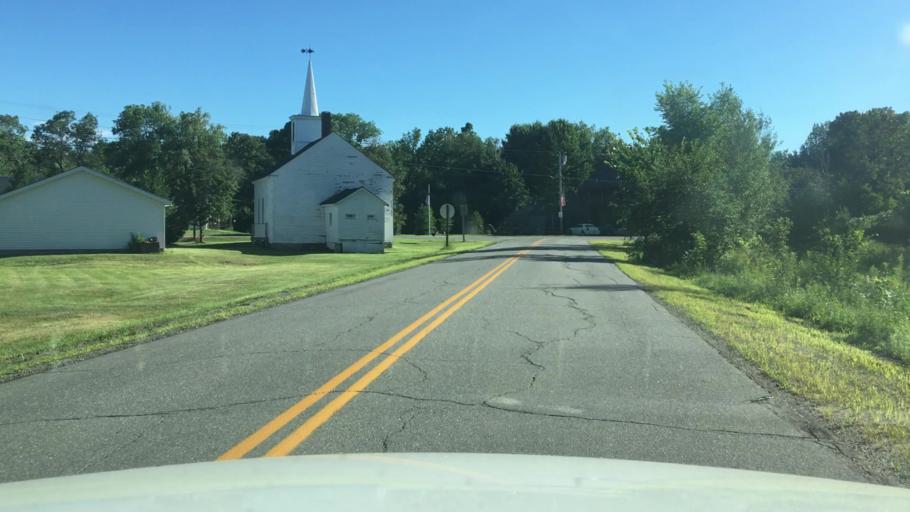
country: US
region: Maine
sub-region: Penobscot County
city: Howland
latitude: 45.1858
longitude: -68.6136
